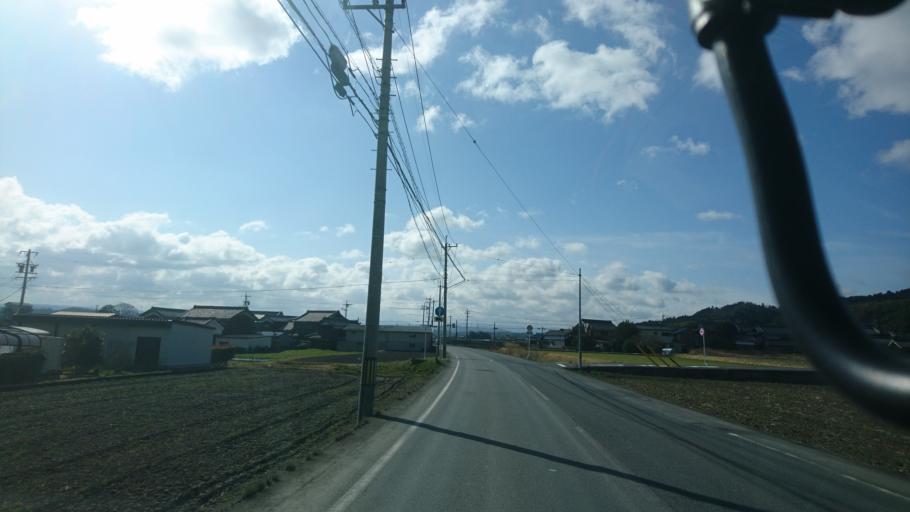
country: JP
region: Mie
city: Ueno-ebisumachi
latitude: 34.7680
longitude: 136.1076
